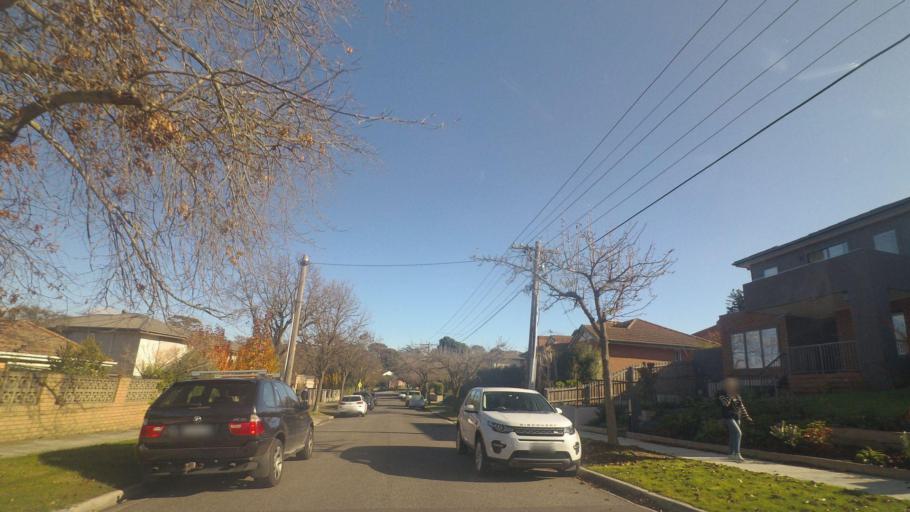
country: AU
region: Victoria
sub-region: Whitehorse
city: Mont Albert North
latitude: -37.8030
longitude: 145.1062
